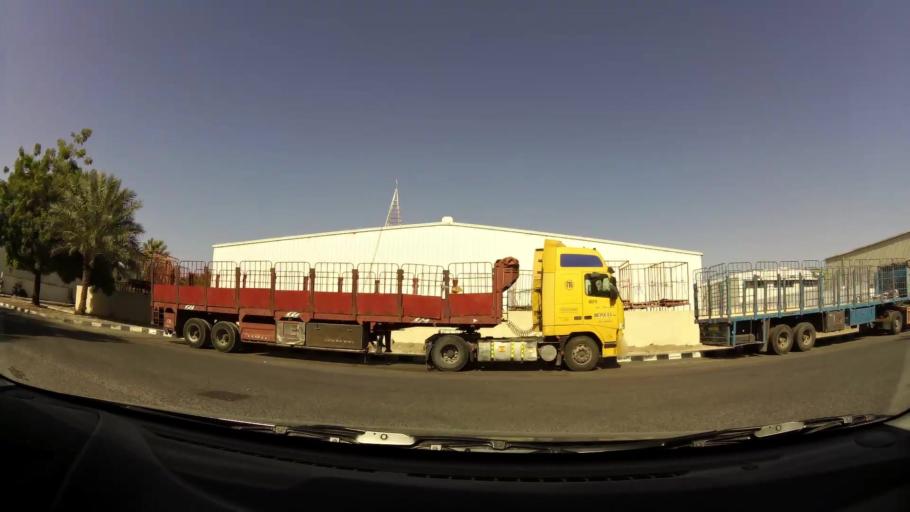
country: OM
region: Muhafazat Masqat
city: As Sib al Jadidah
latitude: 23.5555
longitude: 58.2073
